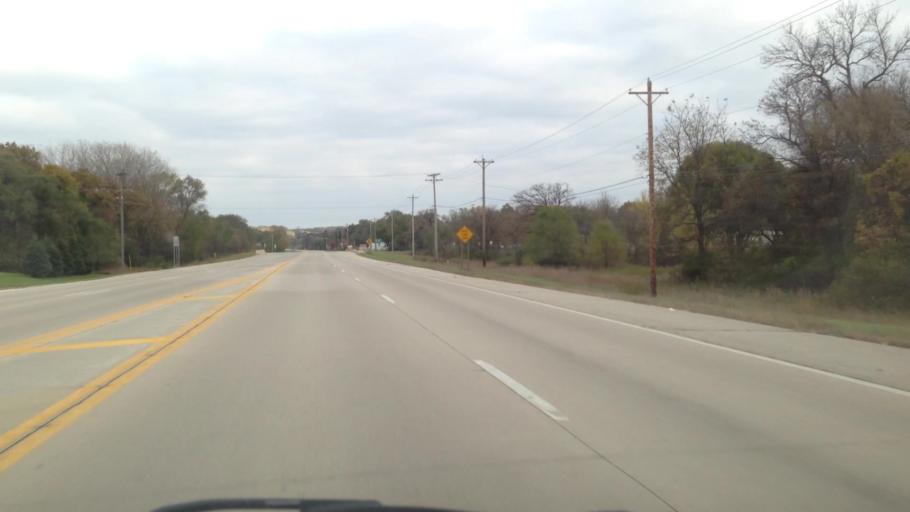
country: US
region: Minnesota
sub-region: Olmsted County
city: Rochester
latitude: 43.9919
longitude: -92.4205
